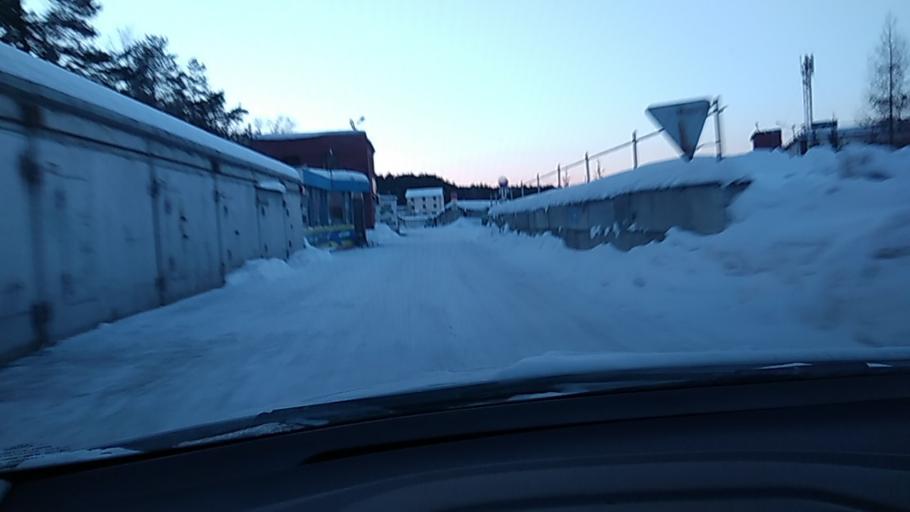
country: RU
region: Sverdlovsk
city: Sovkhoznyy
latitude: 56.7922
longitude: 60.5674
